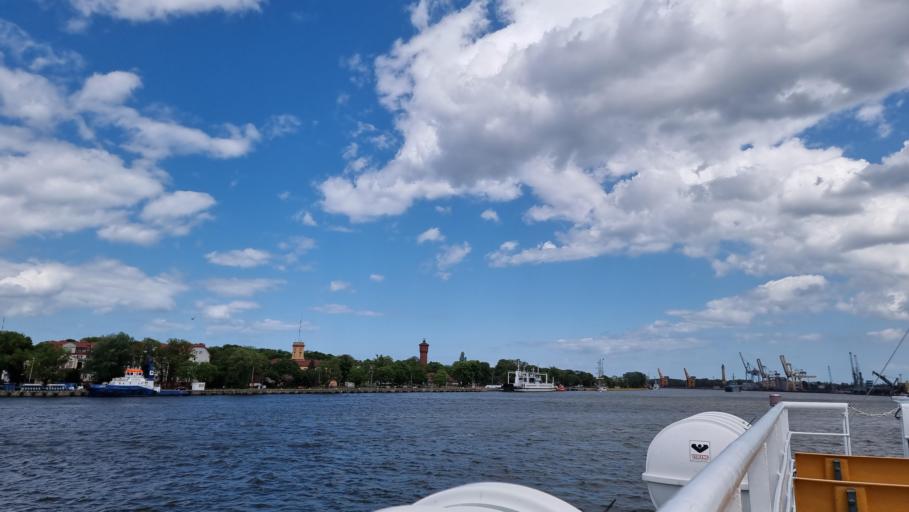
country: PL
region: West Pomeranian Voivodeship
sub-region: Swinoujscie
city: Swinoujscie
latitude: 53.9053
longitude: 14.2613
